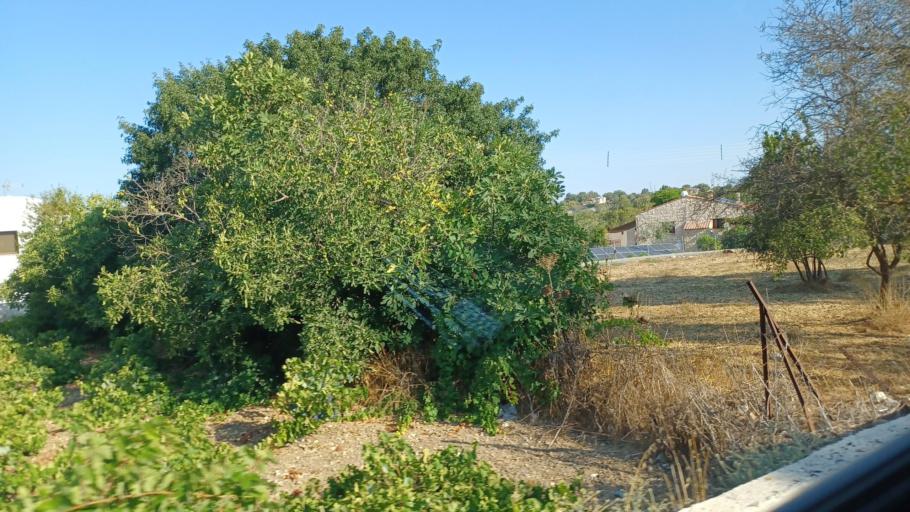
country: CY
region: Pafos
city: Mesogi
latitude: 34.8908
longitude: 32.5110
